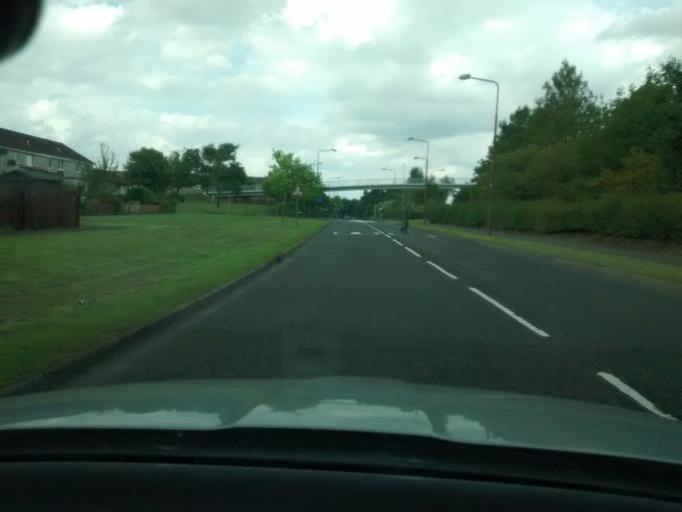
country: GB
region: Scotland
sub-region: West Lothian
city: Livingston
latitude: 55.9004
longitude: -3.5116
